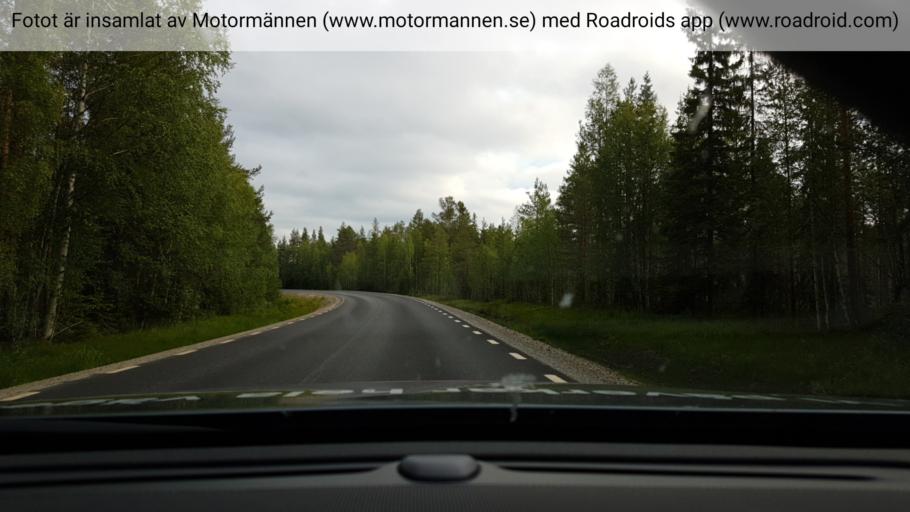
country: SE
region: Vaesterbotten
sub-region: Norsjo Kommun
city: Norsjoe
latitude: 64.4675
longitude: 19.3271
